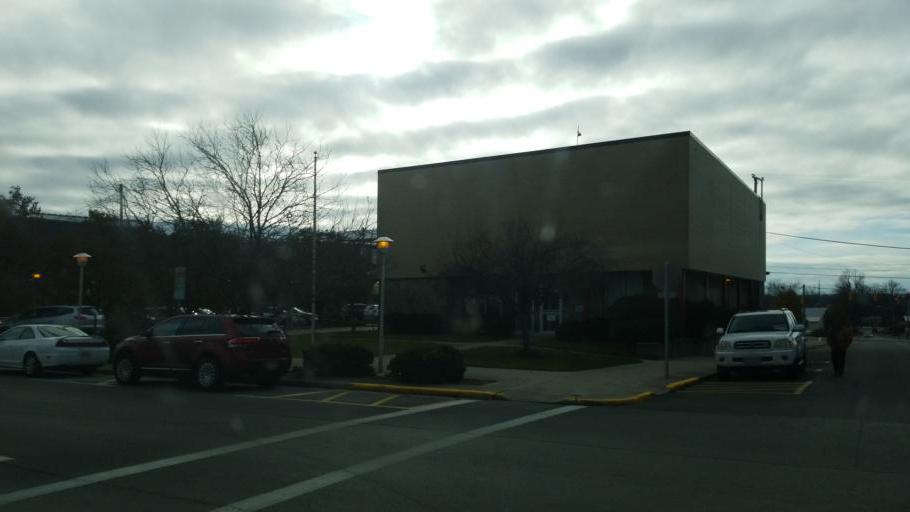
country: US
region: Ohio
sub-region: Hardin County
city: Kenton
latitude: 40.6482
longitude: -83.6105
